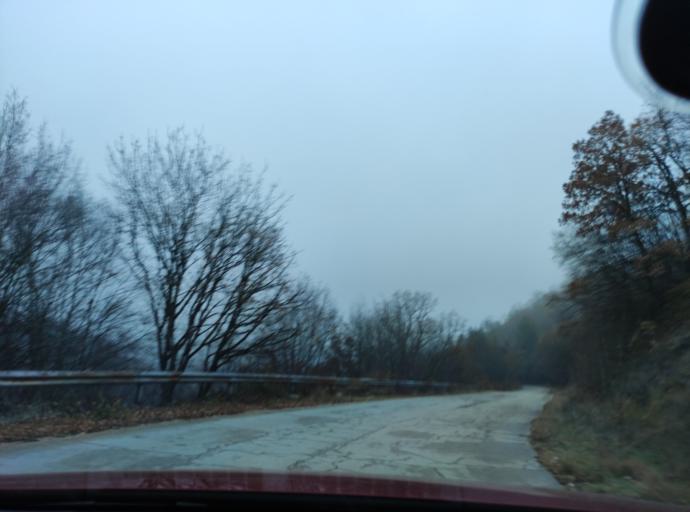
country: BG
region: Lovech
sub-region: Obshtina Yablanitsa
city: Yablanitsa
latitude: 43.1036
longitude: 24.0709
